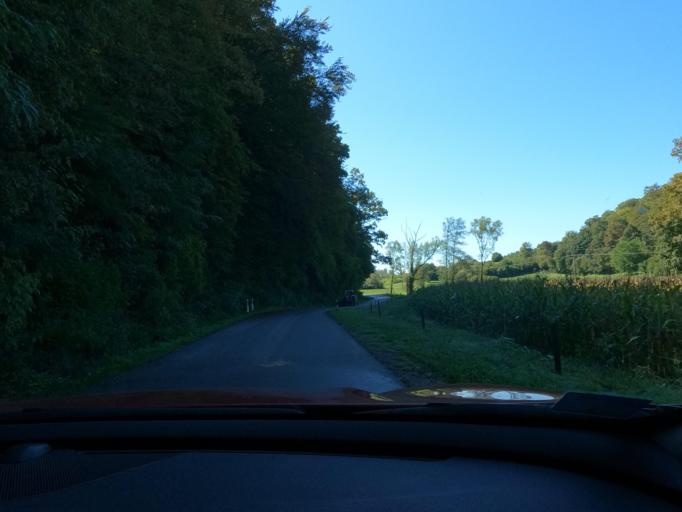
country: HR
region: Sisacko-Moslavacka
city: Petrinja
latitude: 45.3859
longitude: 16.2492
